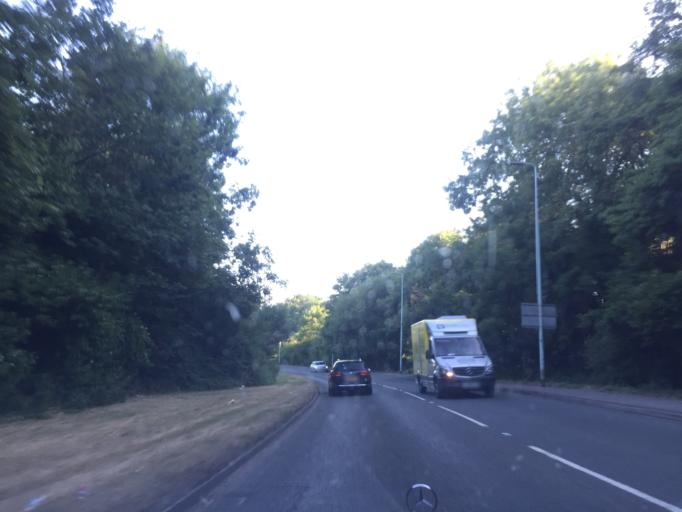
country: GB
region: England
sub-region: Bracknell Forest
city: Sandhurst
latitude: 51.3433
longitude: -0.7869
